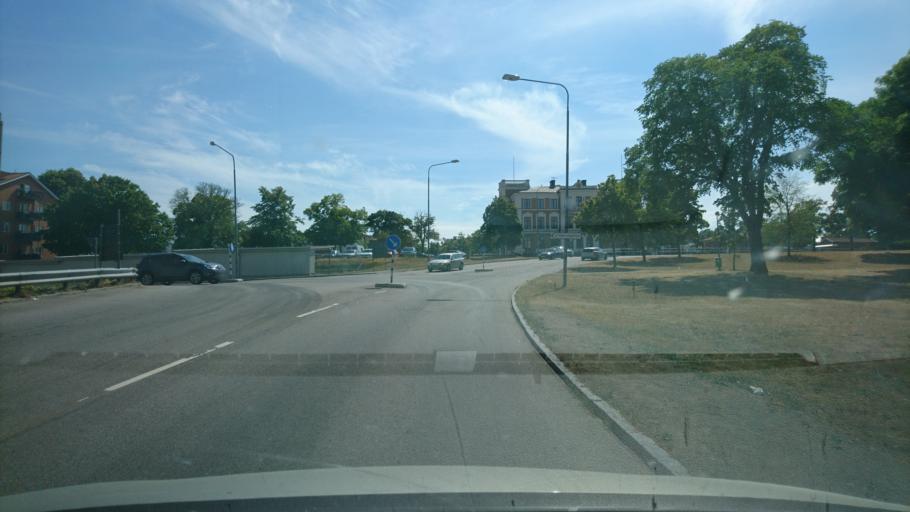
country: SE
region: Kalmar
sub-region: Vasterviks Kommun
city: Vaestervik
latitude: 57.7570
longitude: 16.6443
